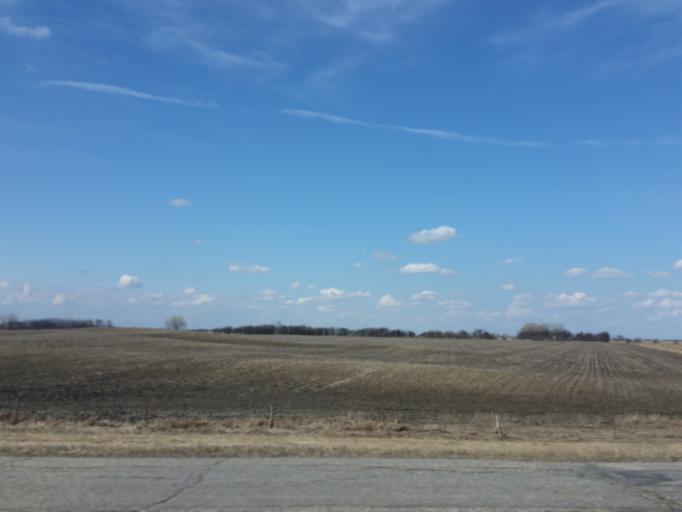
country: US
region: Minnesota
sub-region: Lac qui Parle County
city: Madison
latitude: 44.9346
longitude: -96.4608
